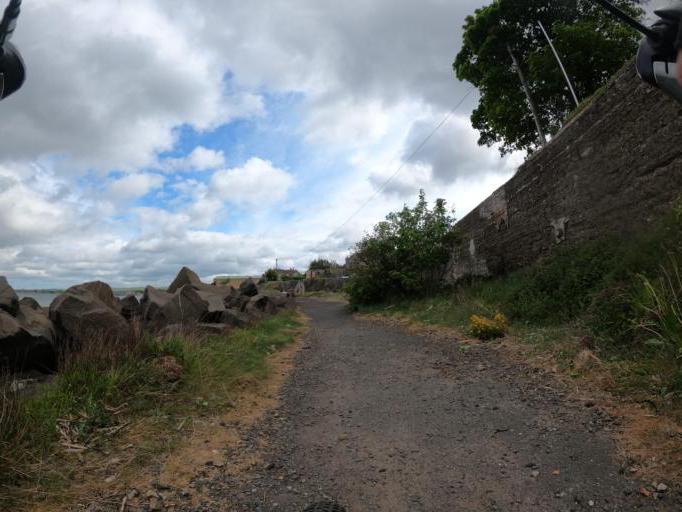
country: GB
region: Scotland
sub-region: East Lothian
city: Musselburgh
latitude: 55.9476
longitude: -3.0808
